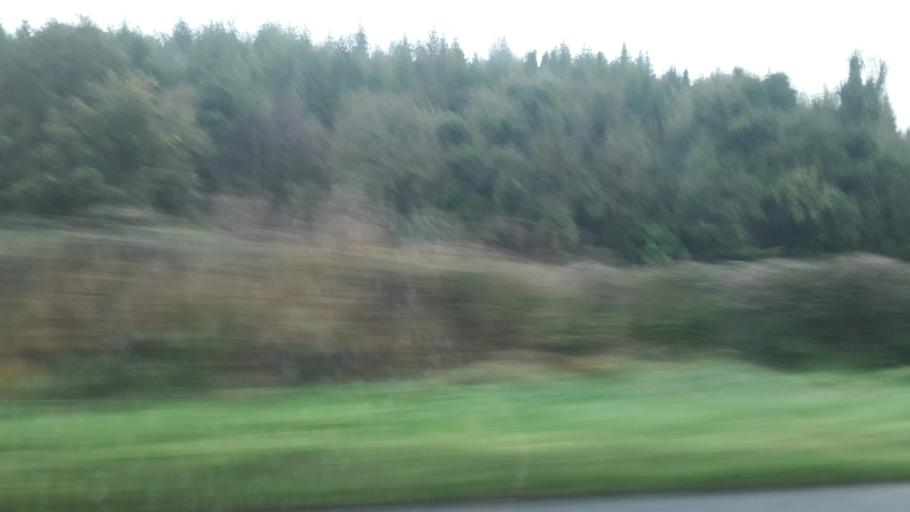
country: IE
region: Leinster
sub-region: An Iarmhi
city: An Muileann gCearr
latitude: 53.6038
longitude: -7.4110
